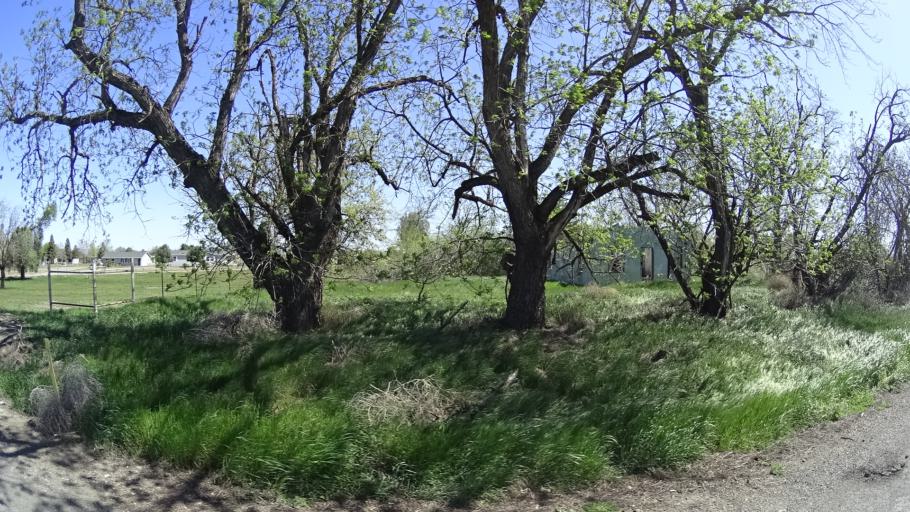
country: US
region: California
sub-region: Glenn County
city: Orland
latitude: 39.7749
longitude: -122.2477
